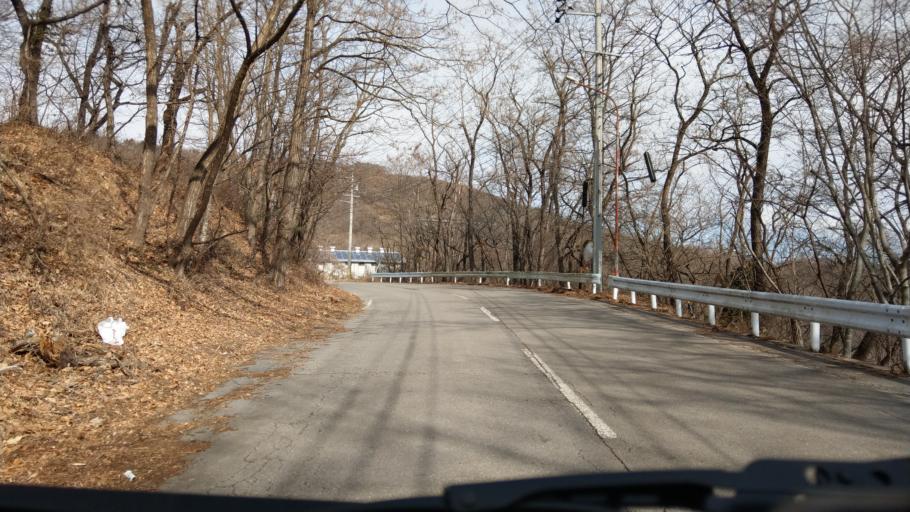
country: JP
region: Nagano
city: Komoro
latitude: 36.2837
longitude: 138.4057
